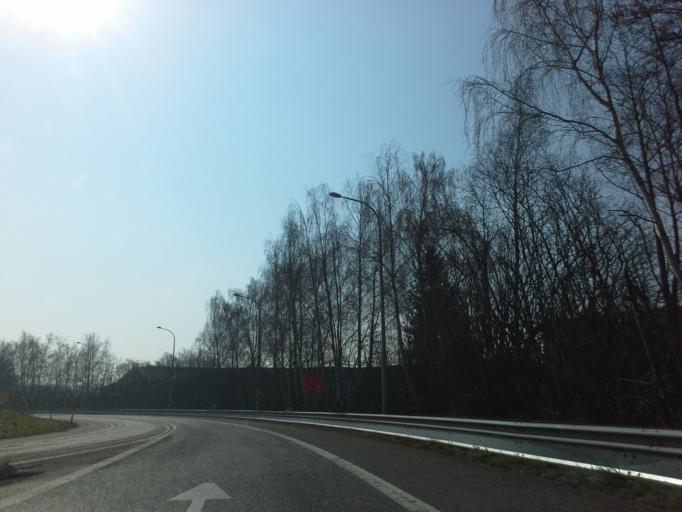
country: BE
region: Flanders
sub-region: Provincie Limburg
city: Hoeselt
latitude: 50.8603
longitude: 5.4957
